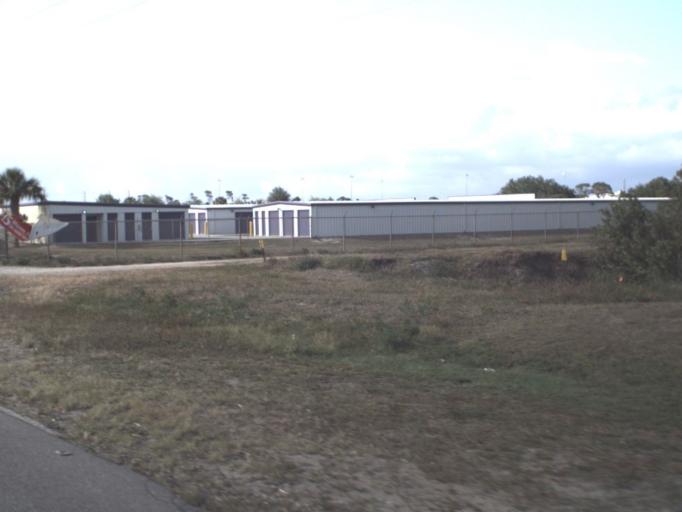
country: US
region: Florida
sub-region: Brevard County
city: Melbourne
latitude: 28.1143
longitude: -80.6361
